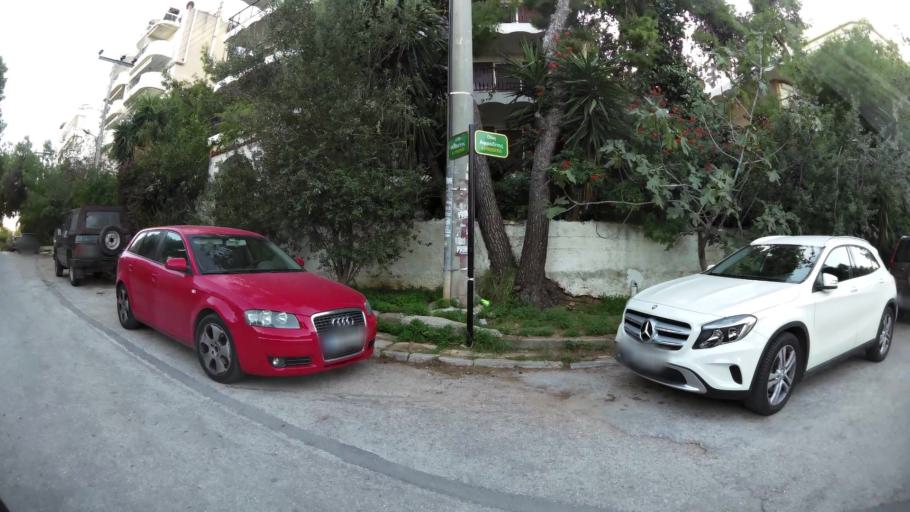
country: GR
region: Attica
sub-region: Nomarchia Anatolikis Attikis
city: Vouliagmeni
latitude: 37.8206
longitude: 23.7947
